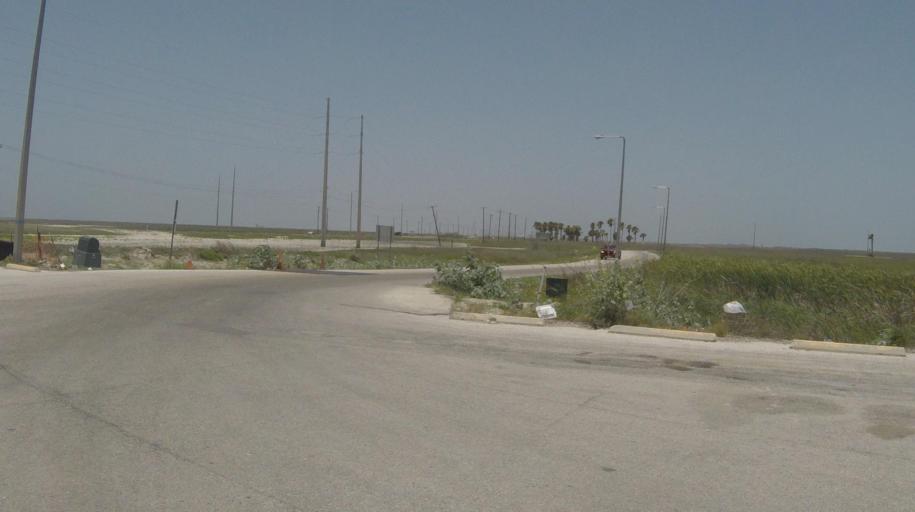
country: US
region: Texas
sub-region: San Patricio County
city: Ingleside
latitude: 27.6192
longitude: -97.2117
